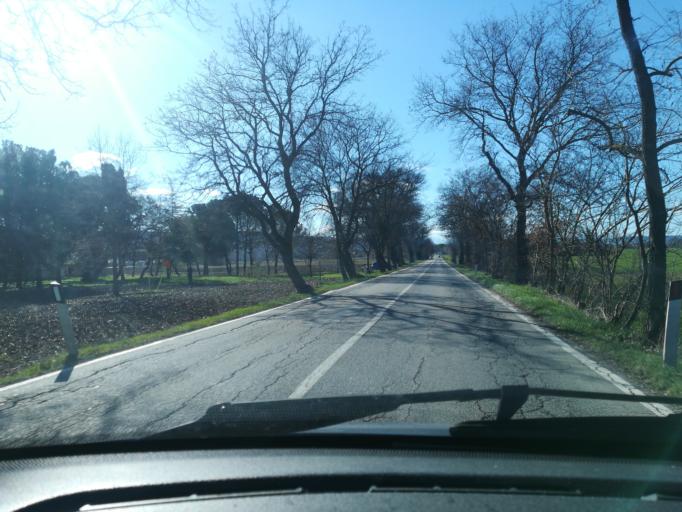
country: IT
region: The Marches
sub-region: Provincia di Macerata
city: Villa Potenza
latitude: 43.3358
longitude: 13.4279
